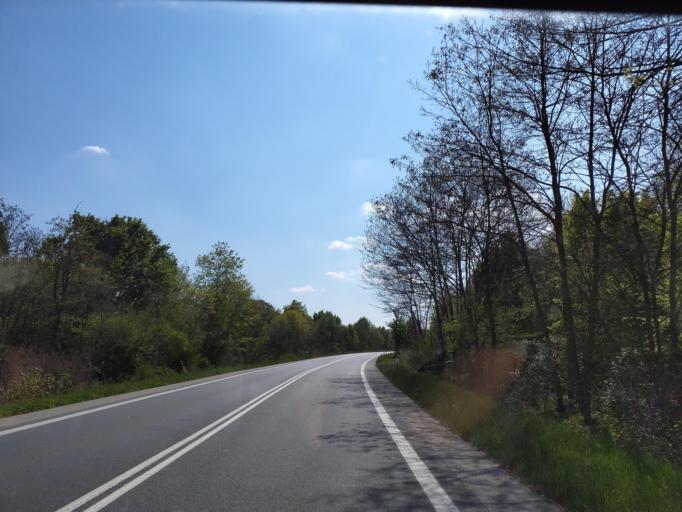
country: IT
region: Piedmont
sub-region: Provincia di Biella
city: Verrone
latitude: 45.4942
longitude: 8.1257
